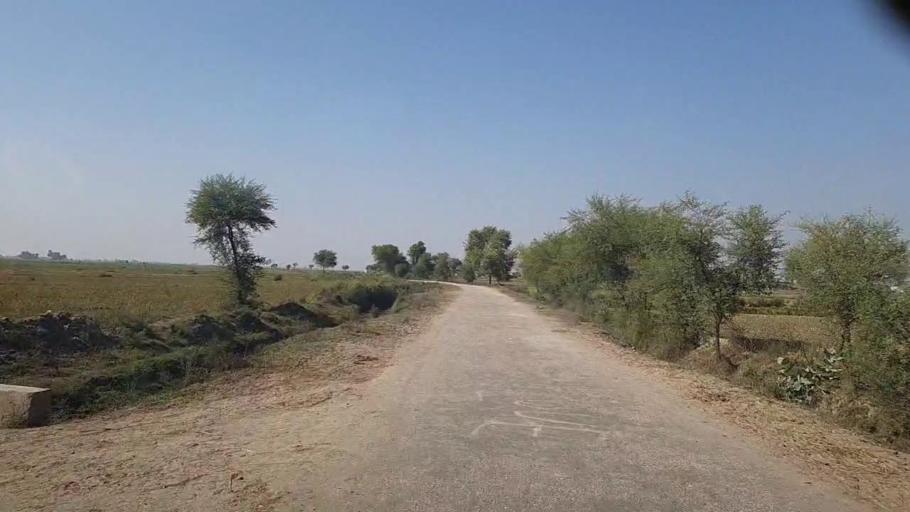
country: PK
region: Sindh
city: Tangwani
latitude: 28.2473
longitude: 68.9460
